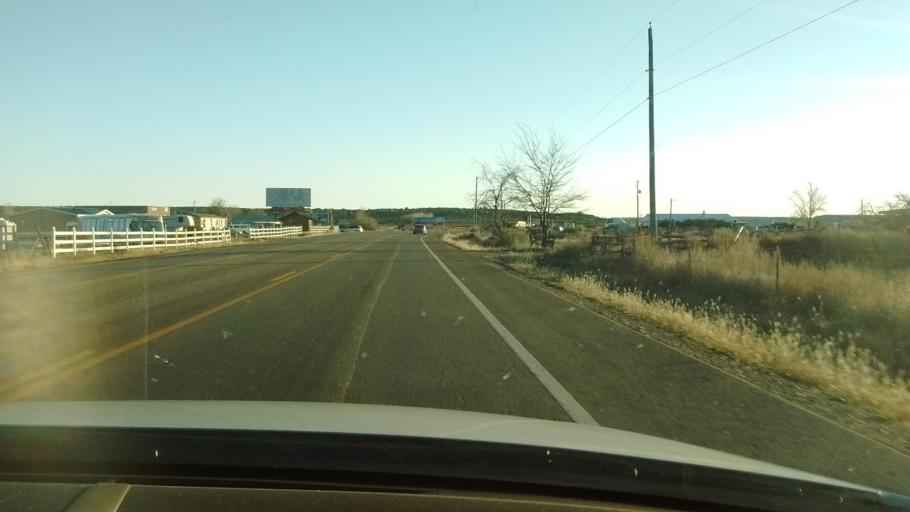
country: US
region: Utah
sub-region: Kane County
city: Kanab
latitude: 37.0152
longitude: -112.5250
